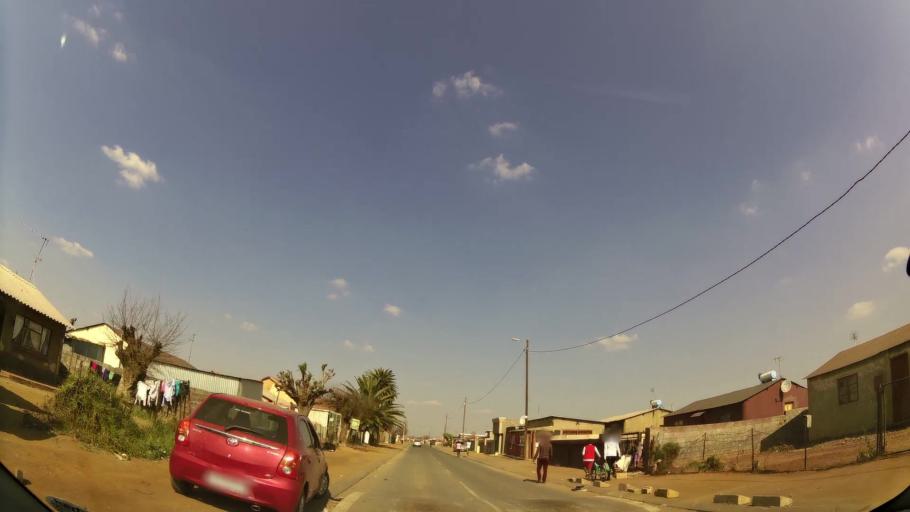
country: ZA
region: Gauteng
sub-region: Ekurhuleni Metropolitan Municipality
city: Benoni
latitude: -26.1474
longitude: 28.4050
